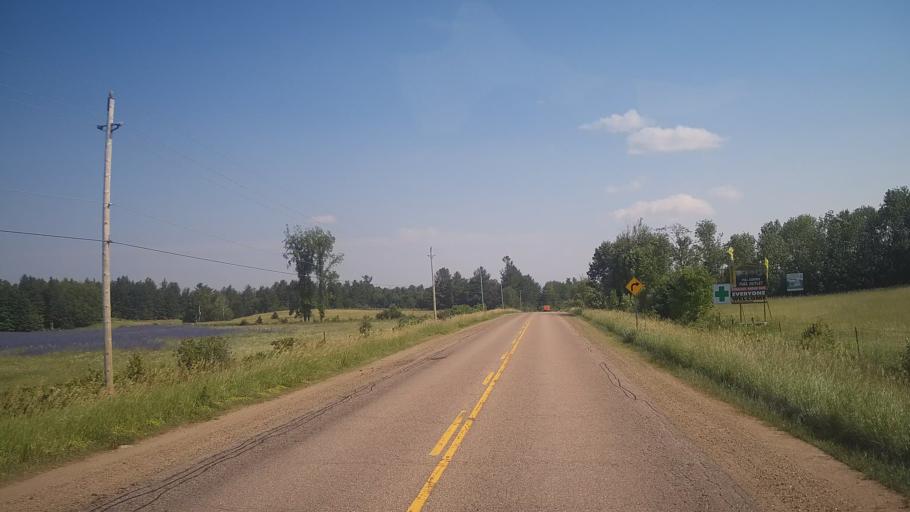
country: CA
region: Ontario
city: Pembroke
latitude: 45.5907
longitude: -77.2278
